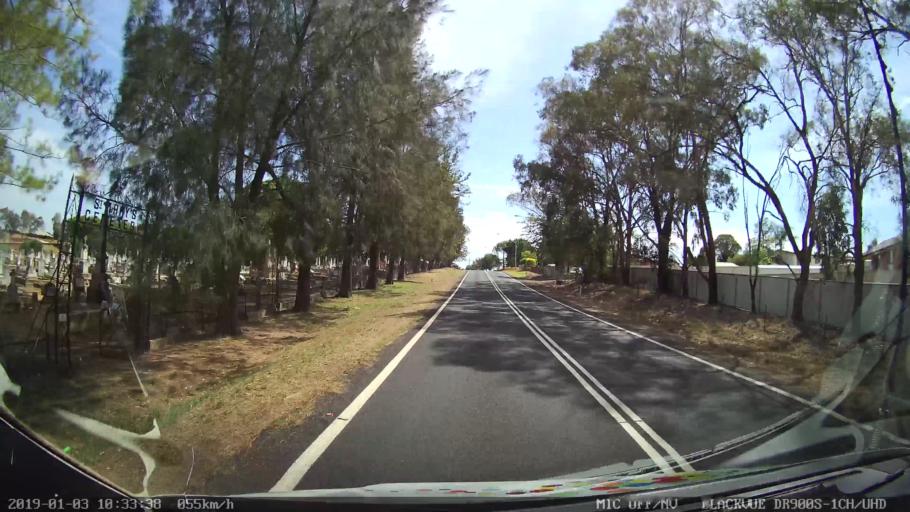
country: AU
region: New South Wales
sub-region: Young
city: Young
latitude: -34.3269
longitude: 148.2889
